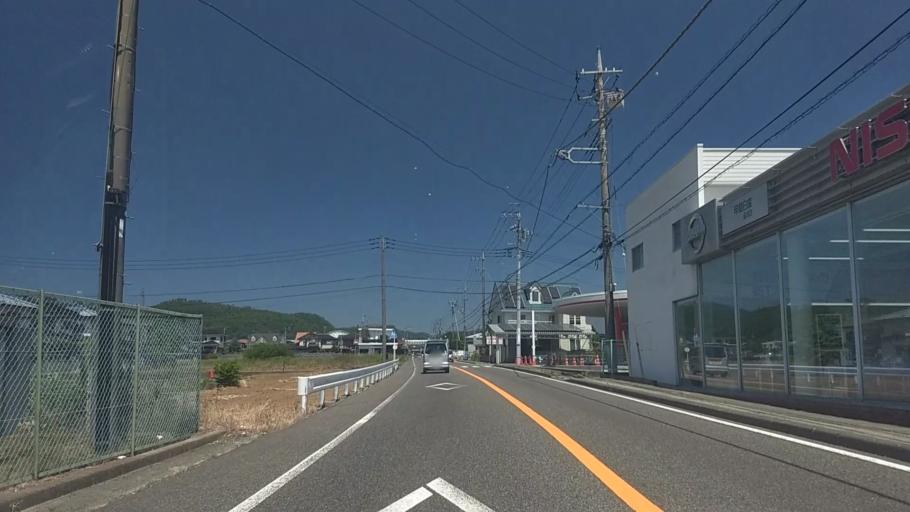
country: JP
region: Yamanashi
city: Nirasaki
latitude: 35.7448
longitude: 138.4409
